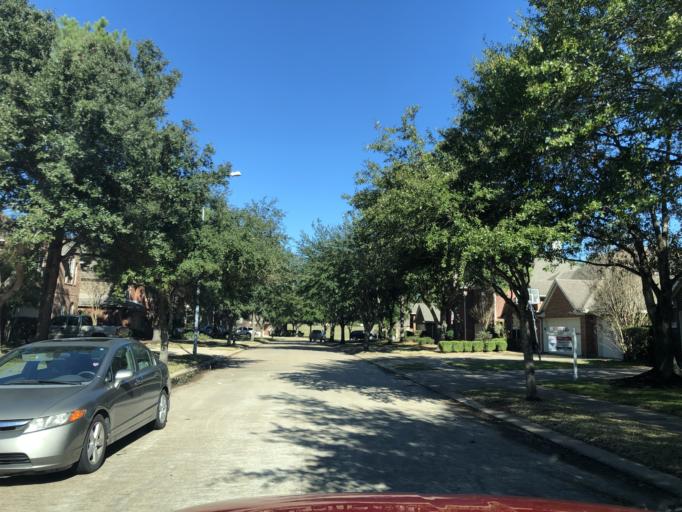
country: US
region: Texas
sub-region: Harris County
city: Oak Cliff Place
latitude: 29.9351
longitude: -95.6639
